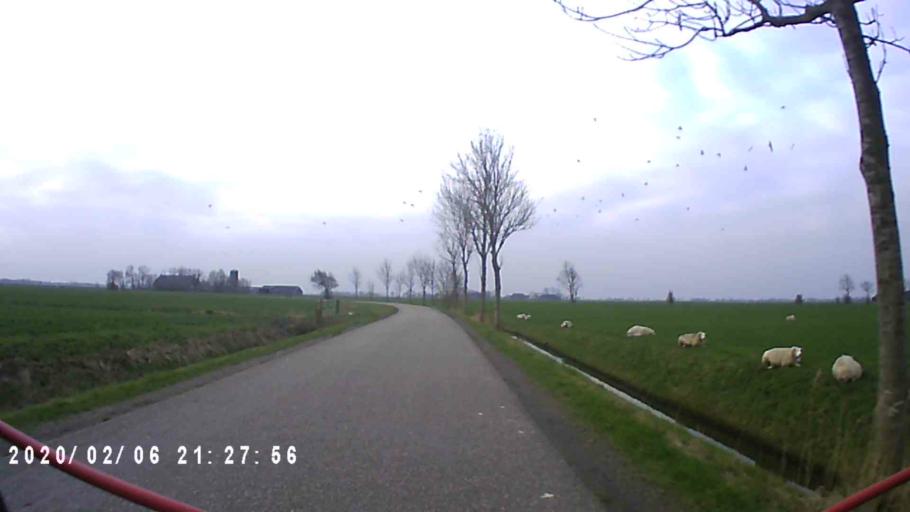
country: NL
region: Groningen
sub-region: Gemeente Zuidhorn
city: Noordhorn
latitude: 53.2823
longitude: 6.3780
